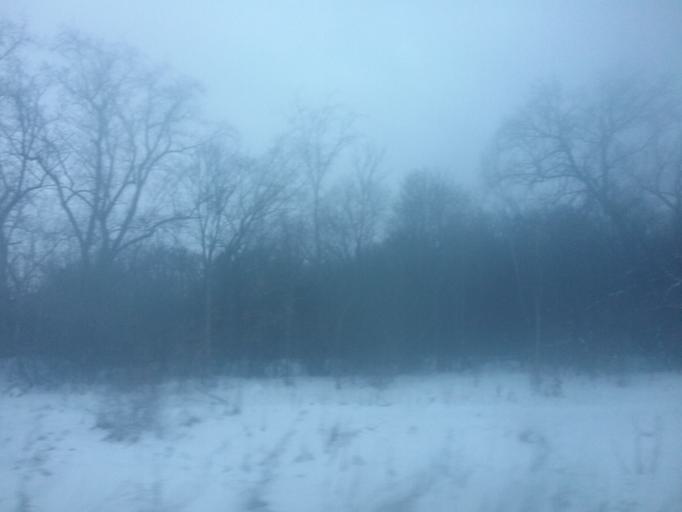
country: RU
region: Tula
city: Bogoroditsk
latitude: 53.8004
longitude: 38.1278
